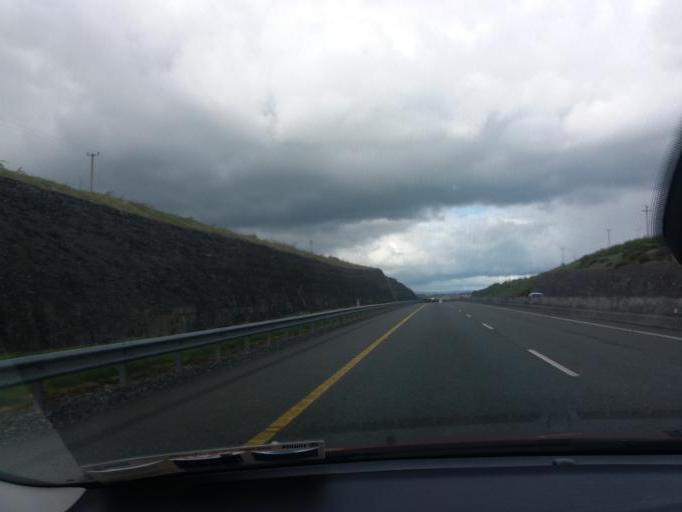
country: IE
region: Leinster
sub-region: Laois
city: Rathdowney
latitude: 52.8251
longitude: -7.4977
